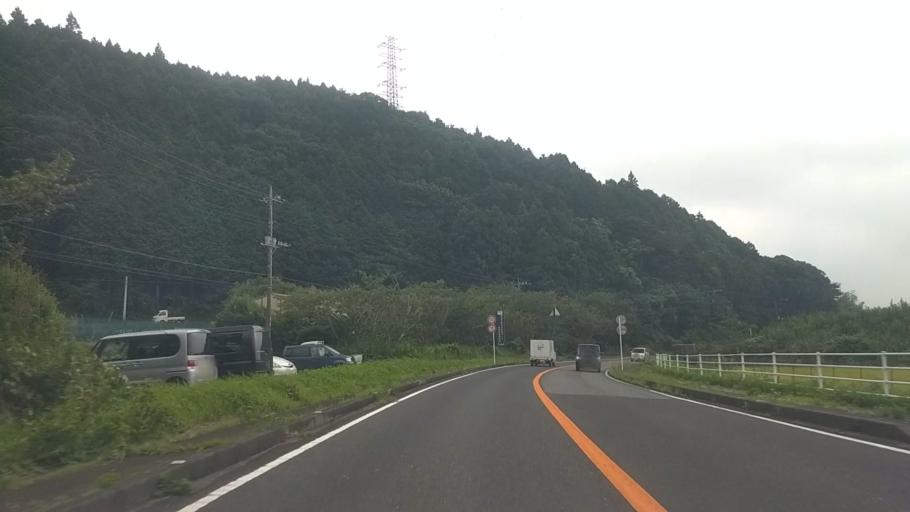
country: JP
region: Chiba
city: Kawaguchi
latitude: 35.1405
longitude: 140.0695
